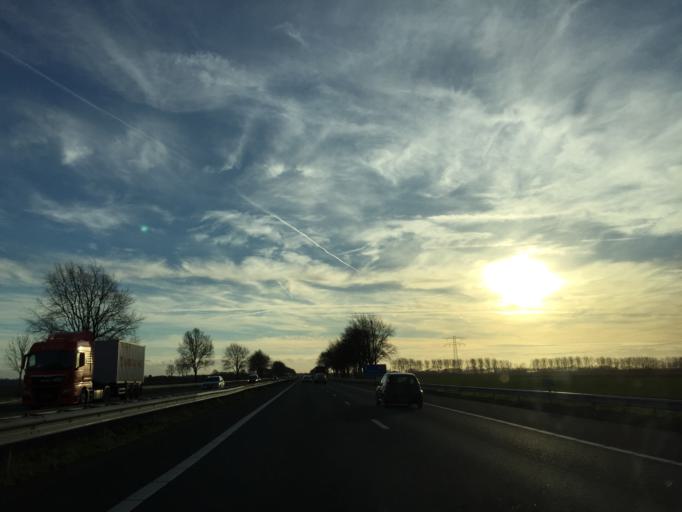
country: NL
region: South Holland
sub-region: Gemeente Oud-Beijerland
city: Oud-Beijerland
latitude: 51.7616
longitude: 4.4192
